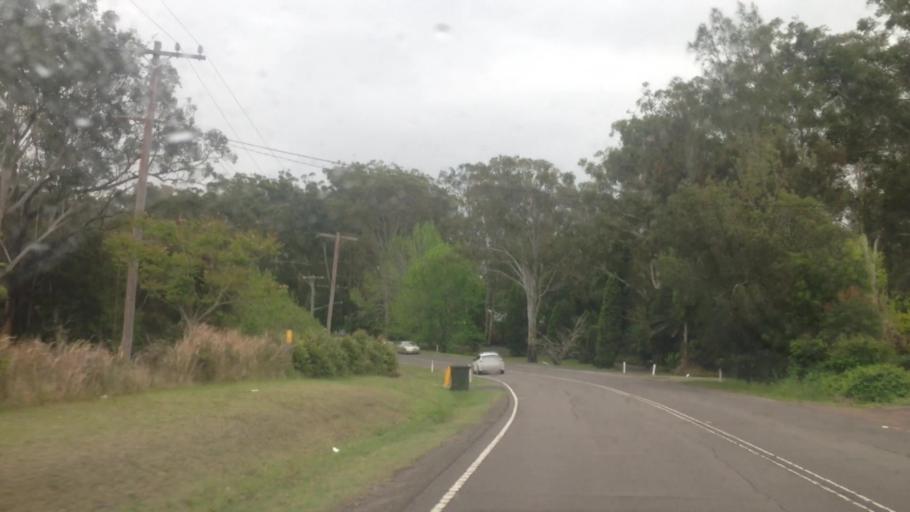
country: AU
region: New South Wales
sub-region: Lake Macquarie Shire
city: Cooranbong
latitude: -33.0958
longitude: 151.4720
